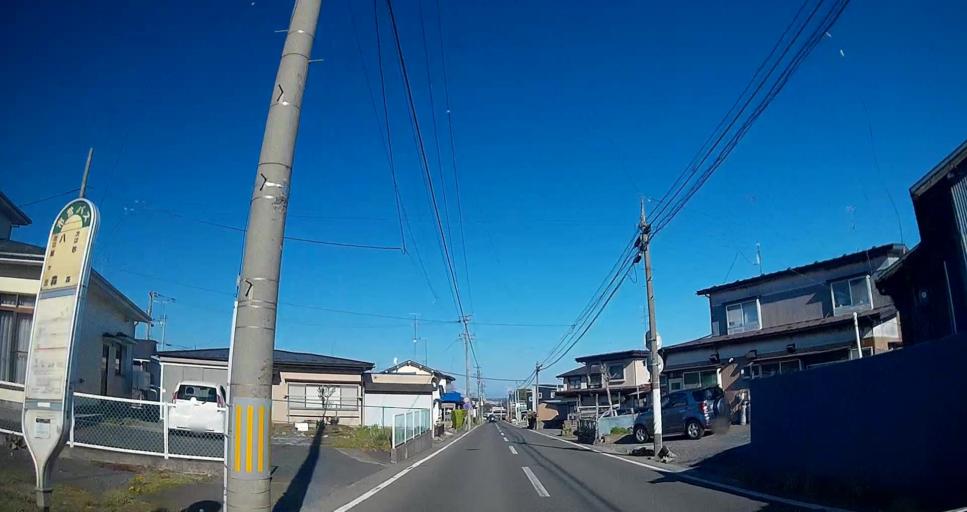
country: JP
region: Aomori
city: Hachinohe
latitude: 40.5236
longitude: 141.5557
